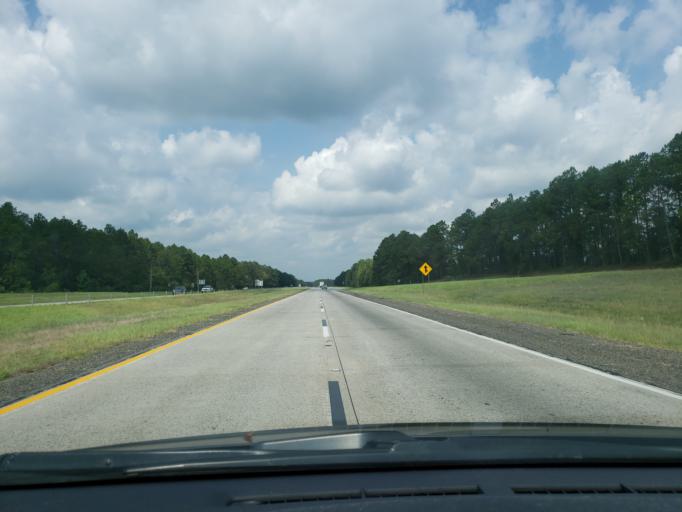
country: US
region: Georgia
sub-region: Treutlen County
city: Soperton
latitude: 32.4342
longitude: -82.6099
